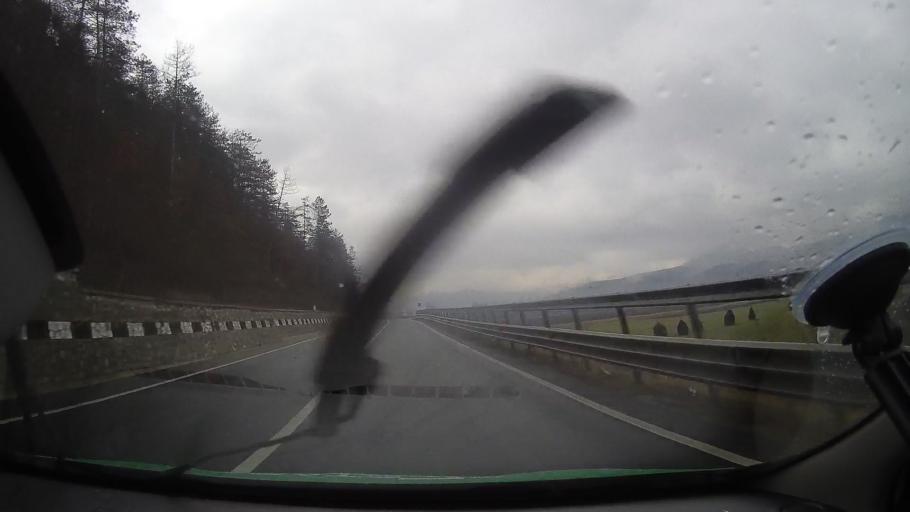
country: RO
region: Hunedoara
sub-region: Comuna Tomesti
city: Tomesti
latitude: 46.1838
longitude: 22.6441
